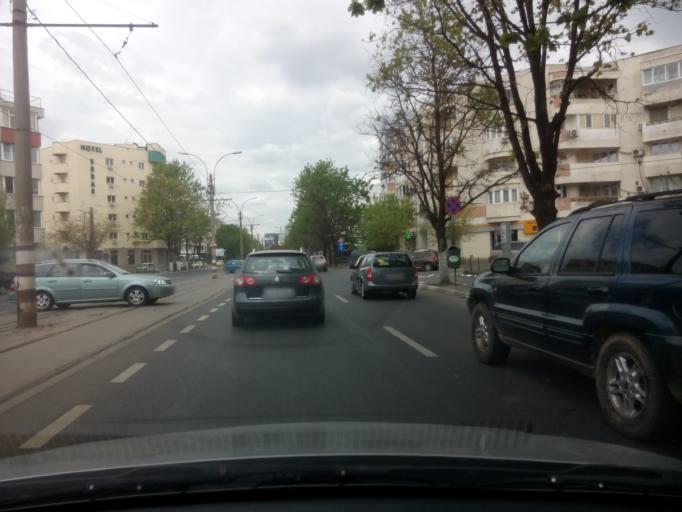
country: RO
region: Bucuresti
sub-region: Municipiul Bucuresti
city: Bucharest
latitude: 44.4834
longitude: 26.0984
